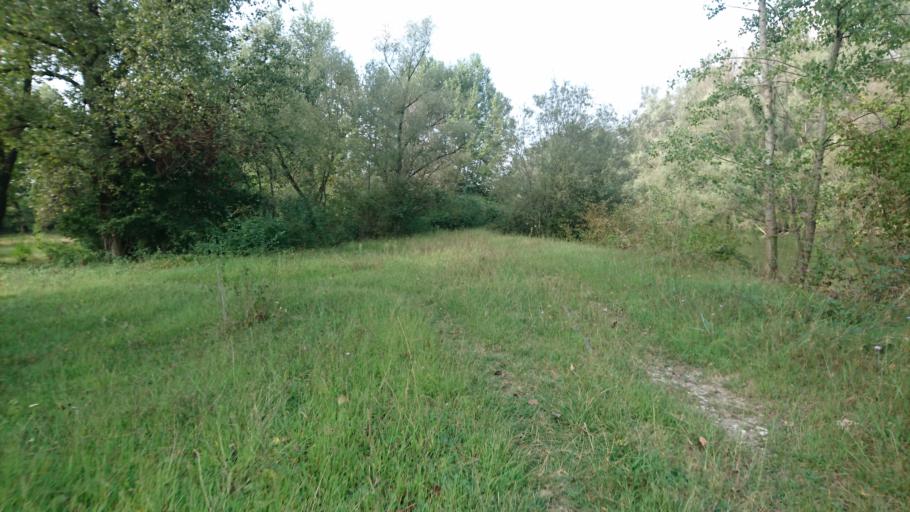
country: IT
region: Veneto
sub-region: Provincia di Padova
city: Grantorto
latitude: 45.6011
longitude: 11.7561
